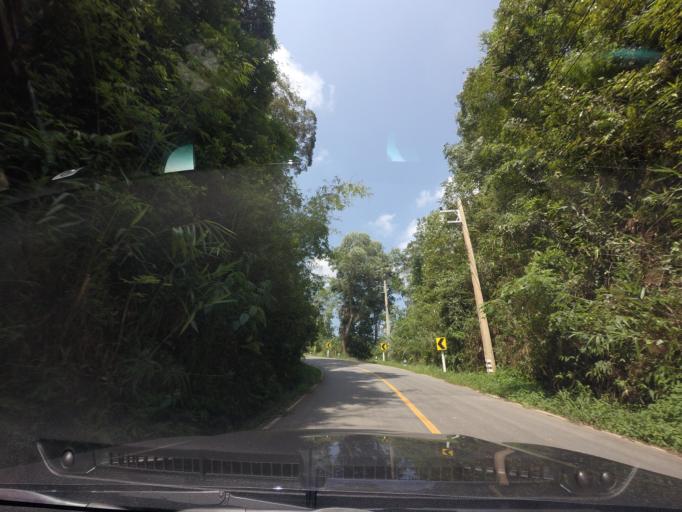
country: TH
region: Loei
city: Na Haeo
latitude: 17.4729
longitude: 100.9377
